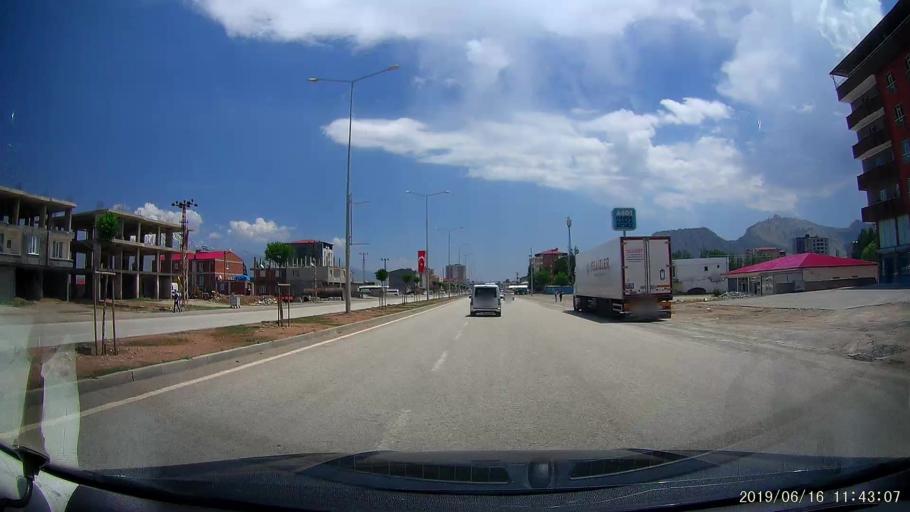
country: TR
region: Agri
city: Dogubayazit
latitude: 39.5570
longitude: 44.0786
